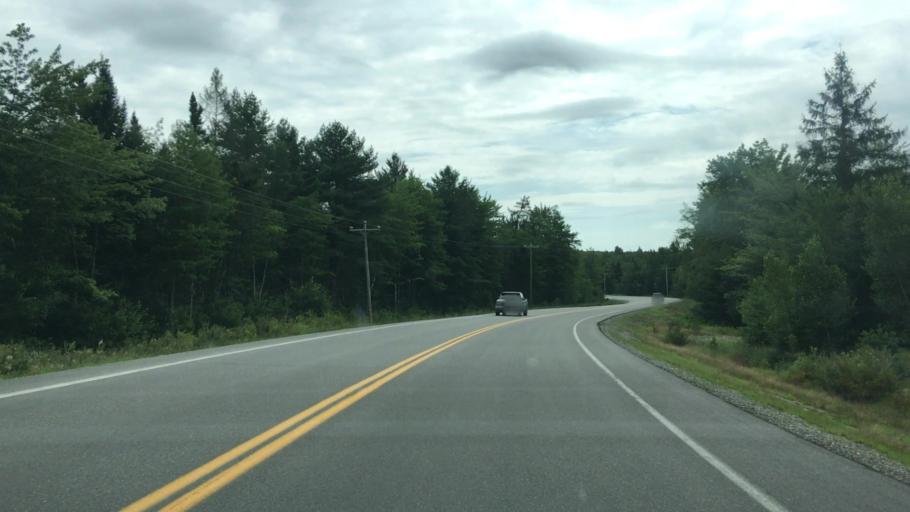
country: US
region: Maine
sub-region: Washington County
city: Machias
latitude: 45.0003
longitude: -67.5707
